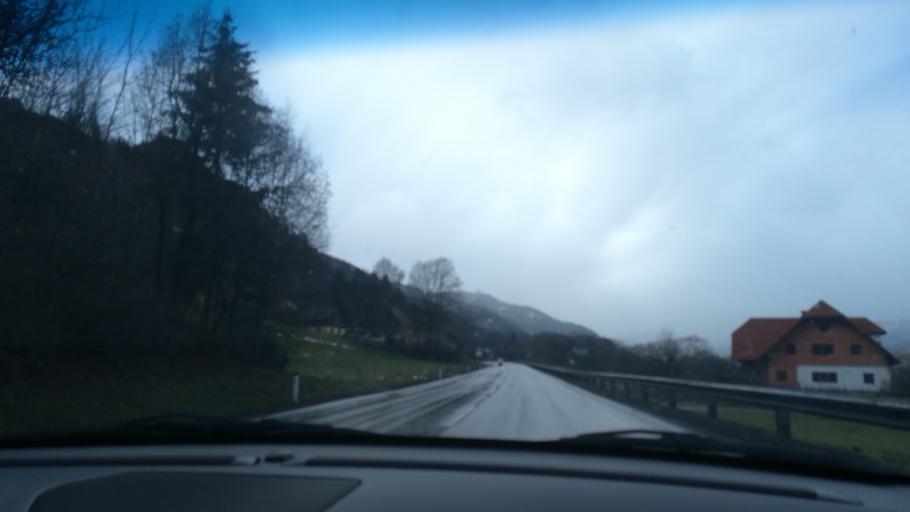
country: AT
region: Styria
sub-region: Politischer Bezirk Murtal
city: Poels
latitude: 47.2038
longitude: 14.5518
